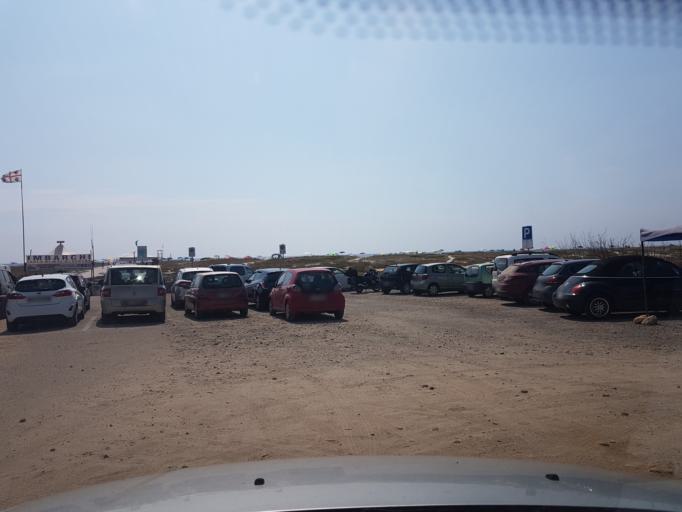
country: IT
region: Sardinia
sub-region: Provincia di Oristano
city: Cabras
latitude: 39.9690
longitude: 8.4005
